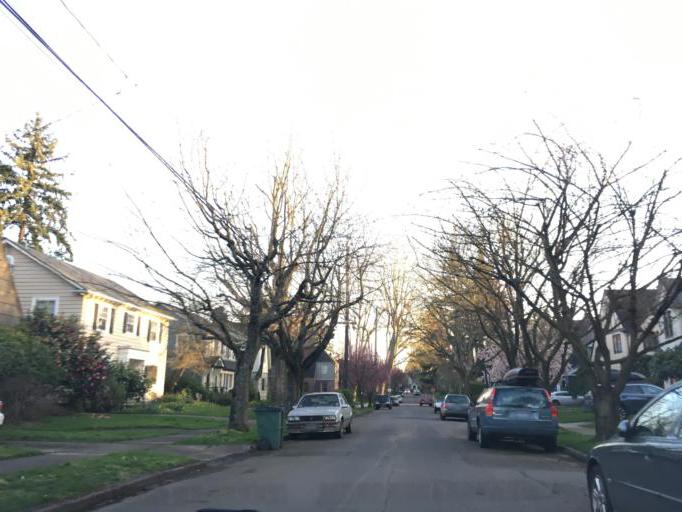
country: US
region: Oregon
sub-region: Multnomah County
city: Portland
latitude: 45.5400
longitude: -122.6345
